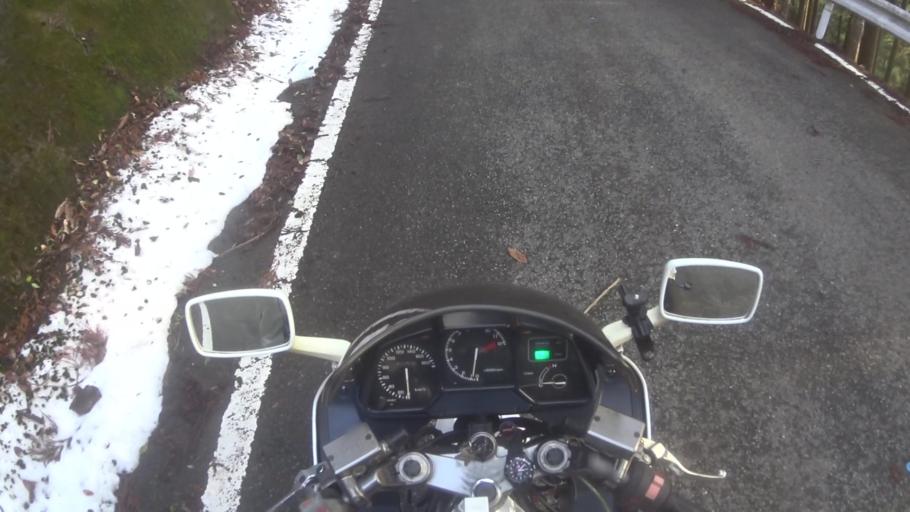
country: JP
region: Kyoto
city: Maizuru
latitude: 35.3563
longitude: 135.4702
